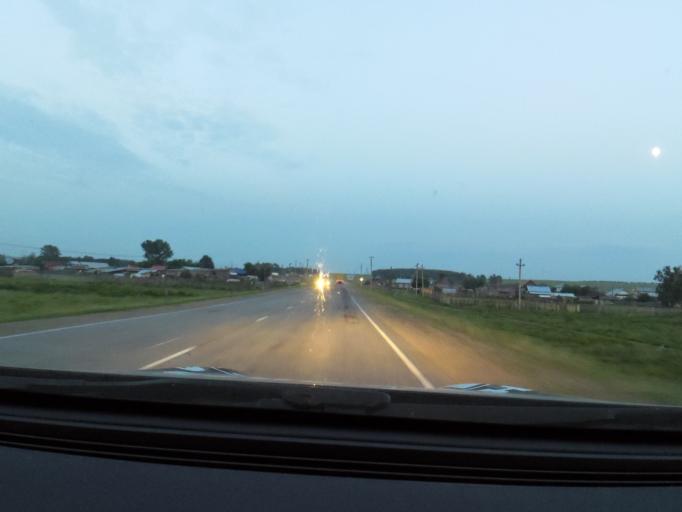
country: RU
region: Bashkortostan
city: Duvan
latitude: 56.1298
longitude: 58.0123
